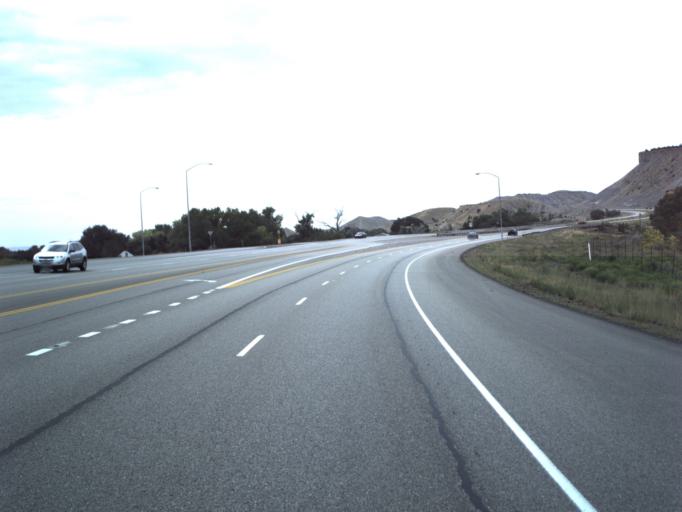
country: US
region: Utah
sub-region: Carbon County
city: Spring Glen
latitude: 39.6423
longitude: -110.8594
